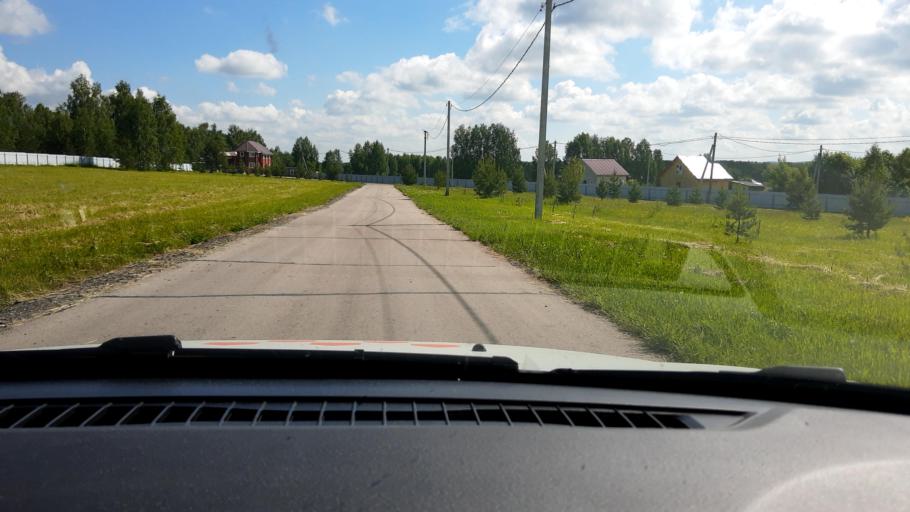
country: RU
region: Nizjnij Novgorod
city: Dal'neye Konstantinovo
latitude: 55.9314
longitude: 43.9984
